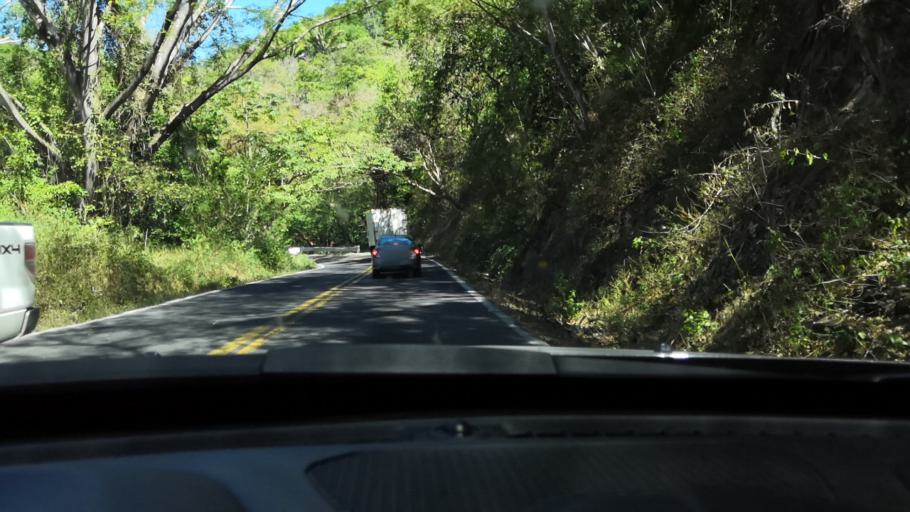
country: MX
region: Nayarit
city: Compostela
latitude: 21.2191
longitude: -104.9972
